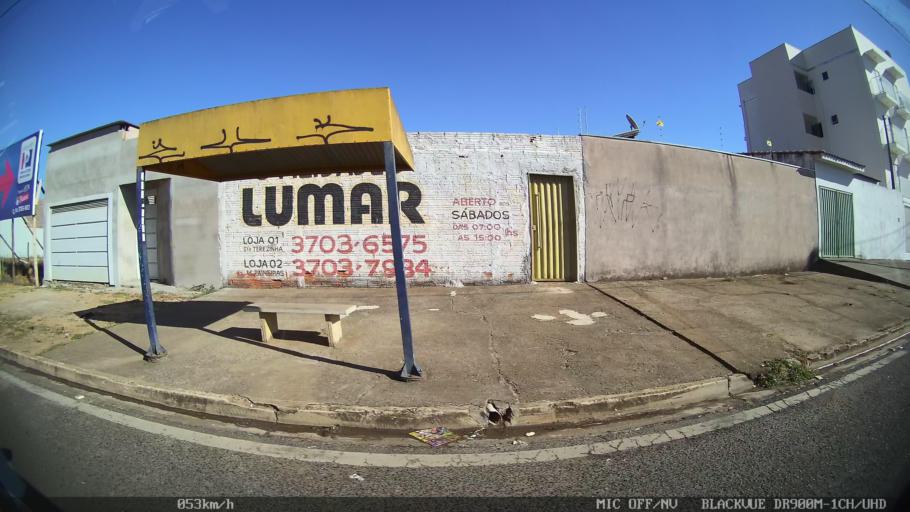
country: BR
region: Sao Paulo
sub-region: Franca
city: Franca
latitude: -20.4783
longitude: -47.4126
